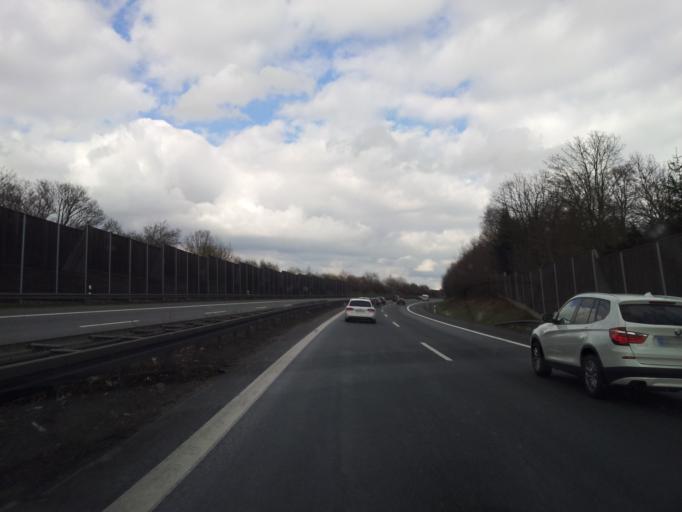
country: DE
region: Saxony
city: Wilkau-Hasslau
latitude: 50.6734
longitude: 12.5326
